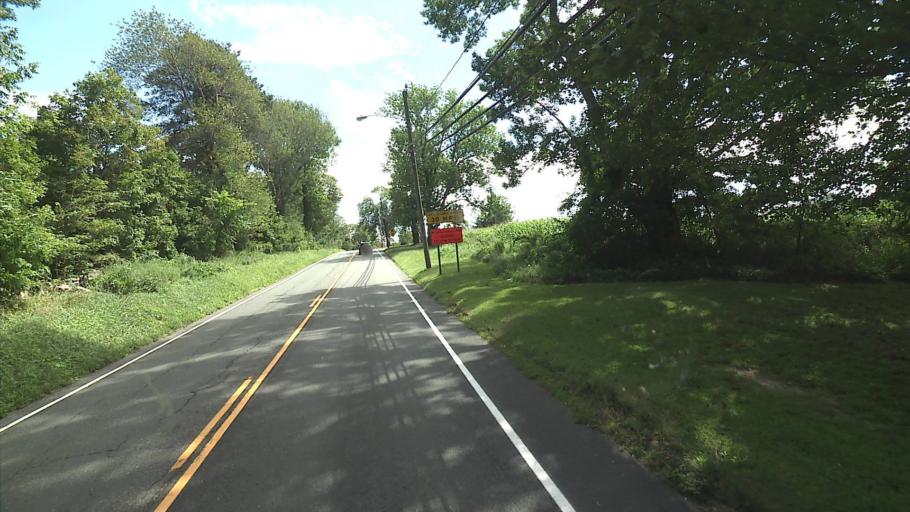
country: US
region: Connecticut
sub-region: Tolland County
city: Storrs
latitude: 41.8200
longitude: -72.2571
